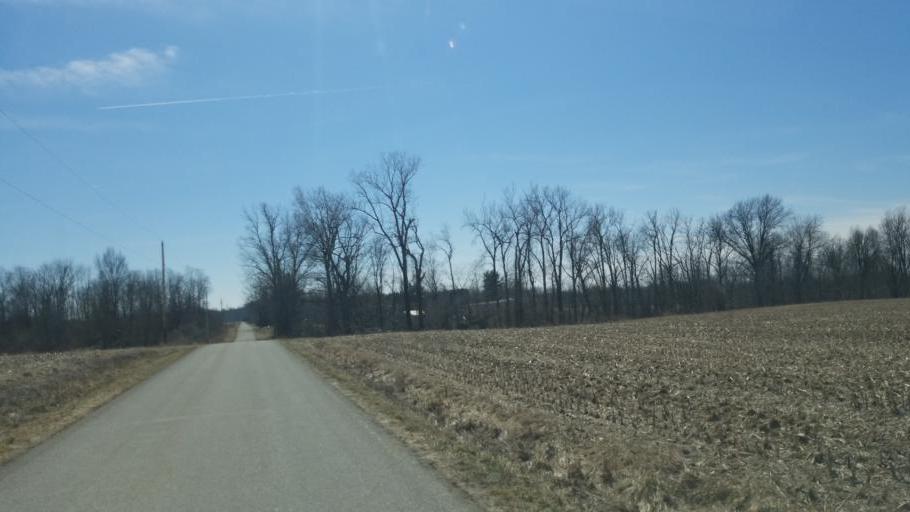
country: US
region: Ohio
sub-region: Crawford County
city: Galion
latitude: 40.6986
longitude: -82.7558
